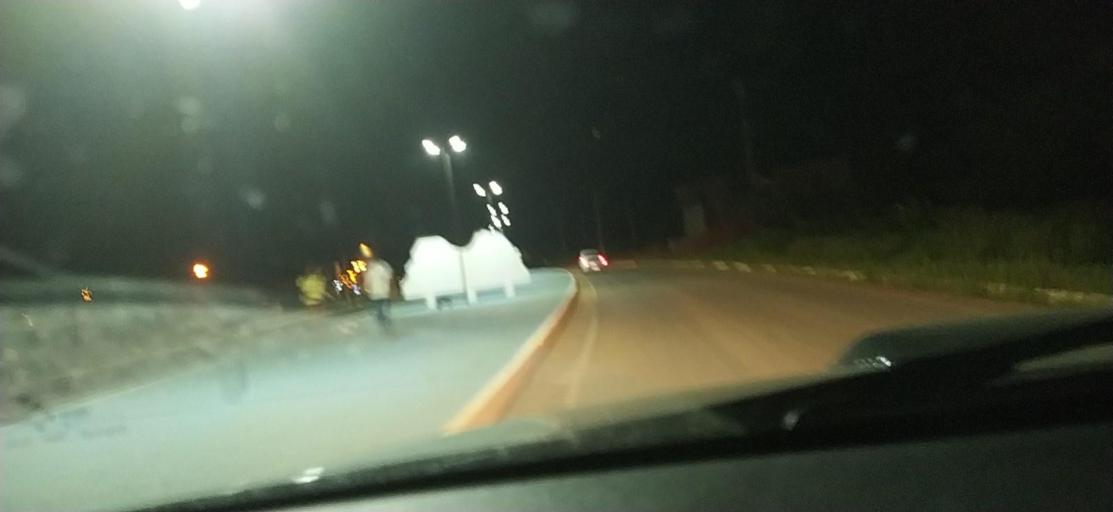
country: BR
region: Minas Gerais
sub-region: Monte Azul
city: Monte Azul
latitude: -15.1608
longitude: -42.8681
